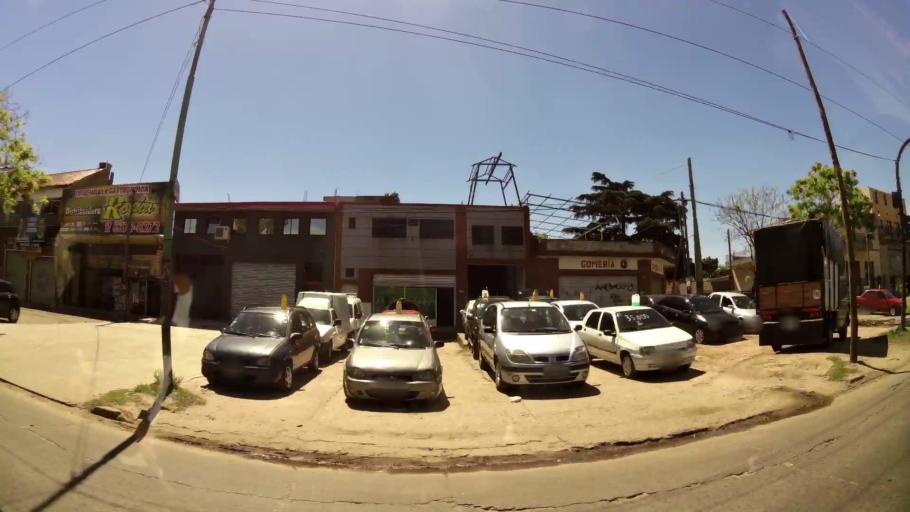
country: AR
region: Buenos Aires
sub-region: Partido de Almirante Brown
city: Adrogue
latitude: -34.7533
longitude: -58.3452
